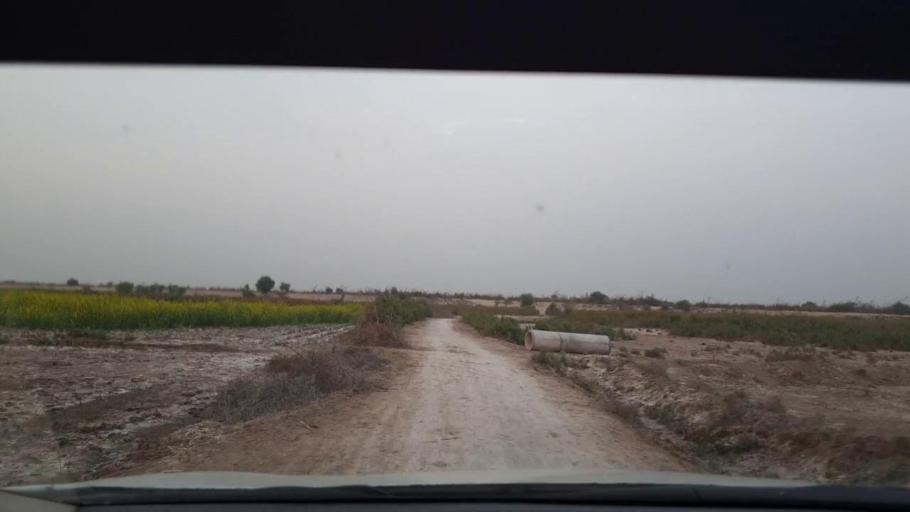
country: PK
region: Sindh
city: Berani
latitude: 25.8690
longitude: 68.7676
